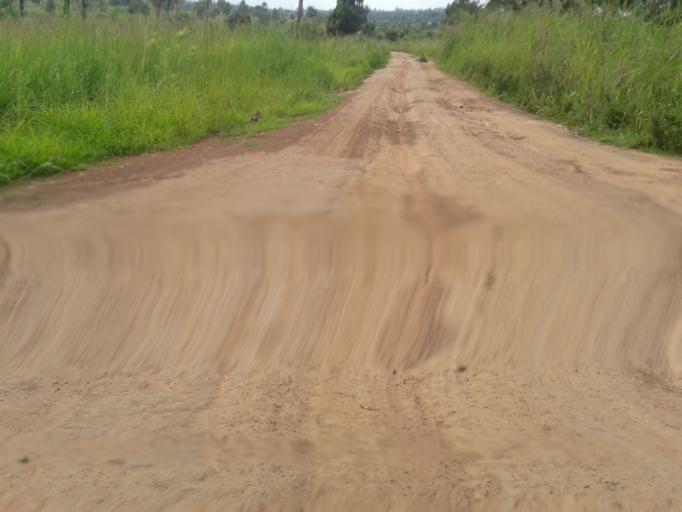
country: UG
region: Northern Region
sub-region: Gulu District
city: Gulu
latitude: 2.8271
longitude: 32.2571
